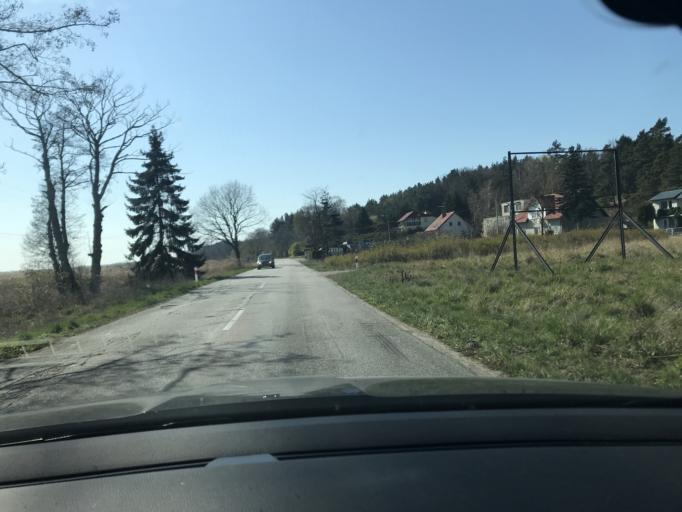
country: PL
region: Pomeranian Voivodeship
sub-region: Powiat nowodworski
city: Sztutowo
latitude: 54.3520
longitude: 19.2924
